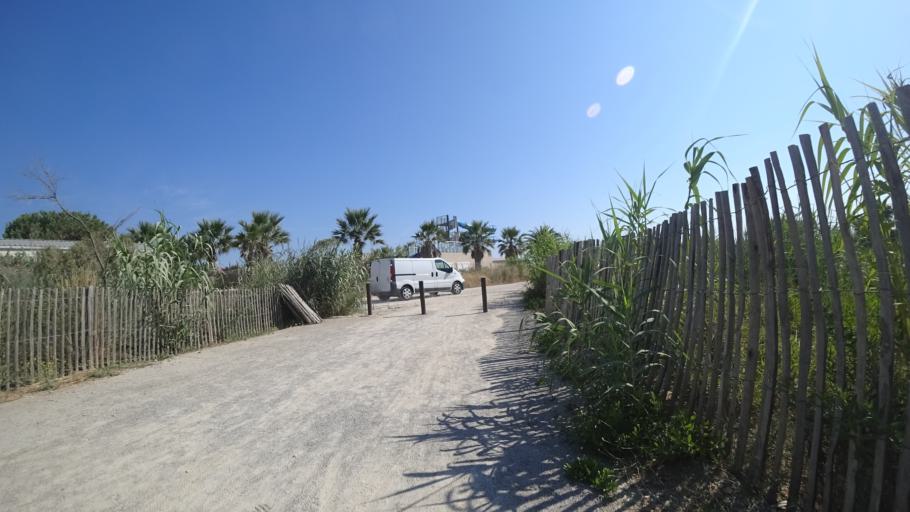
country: FR
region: Languedoc-Roussillon
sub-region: Departement des Pyrenees-Orientales
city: Le Barcares
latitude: 42.7689
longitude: 3.0345
